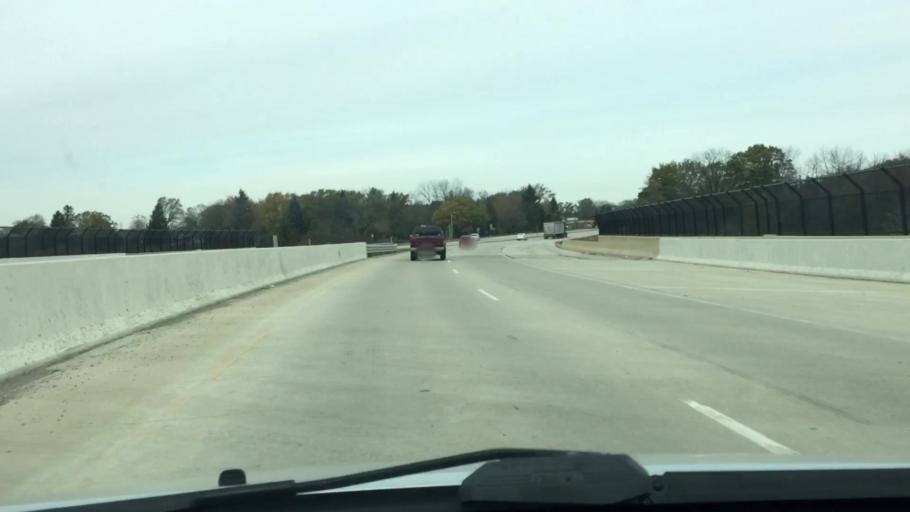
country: US
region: Wisconsin
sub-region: Milwaukee County
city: Hales Corners
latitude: 42.9141
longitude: -88.0446
